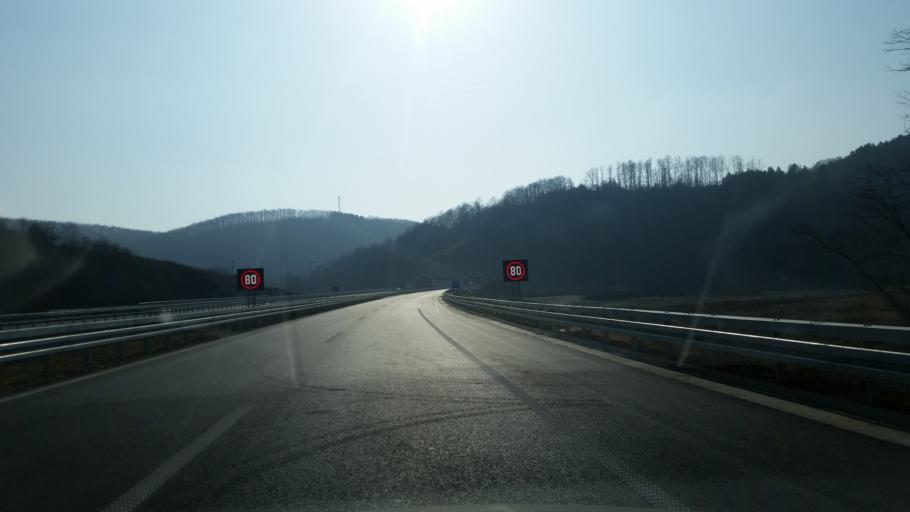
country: RS
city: Prislonica
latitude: 43.9848
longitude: 20.4024
